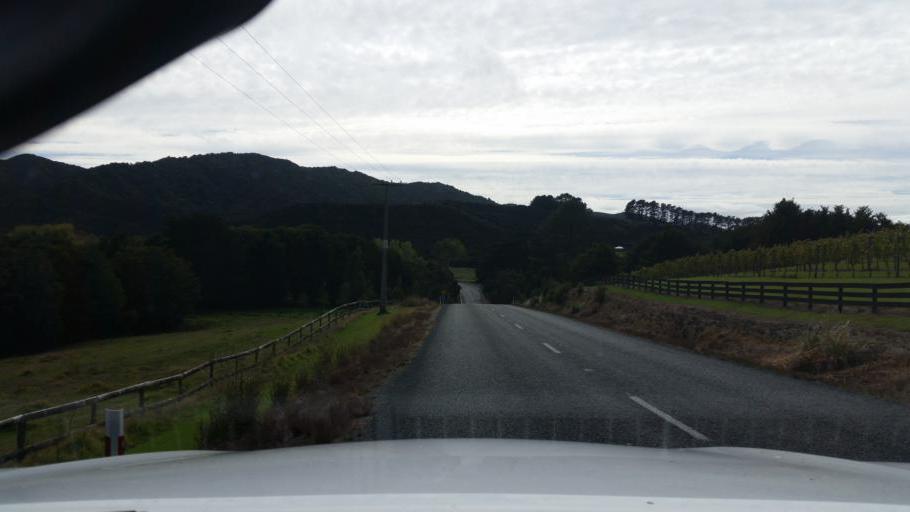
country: NZ
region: Auckland
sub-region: Auckland
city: Wellsford
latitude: -36.0887
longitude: 174.5342
